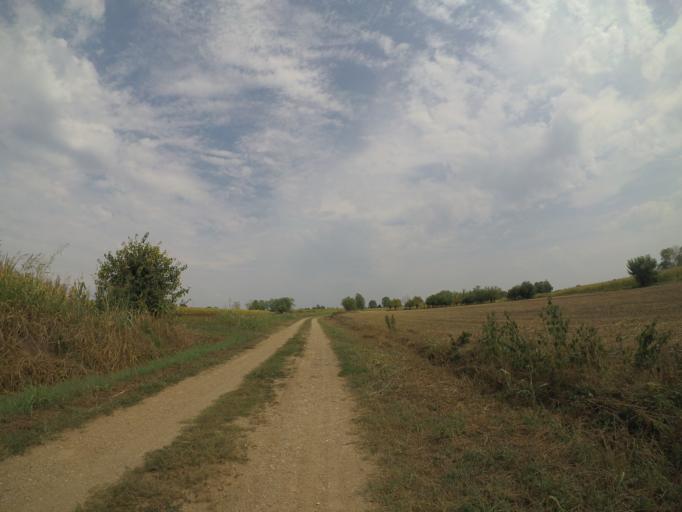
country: IT
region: Friuli Venezia Giulia
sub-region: Provincia di Udine
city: Talmassons
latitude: 45.9313
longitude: 13.1312
